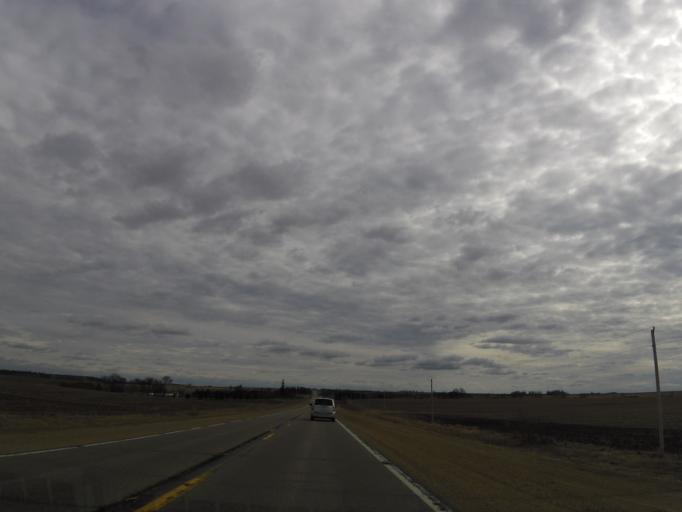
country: US
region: Iowa
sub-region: Chickasaw County
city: New Hampton
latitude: 43.2178
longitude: -92.2986
